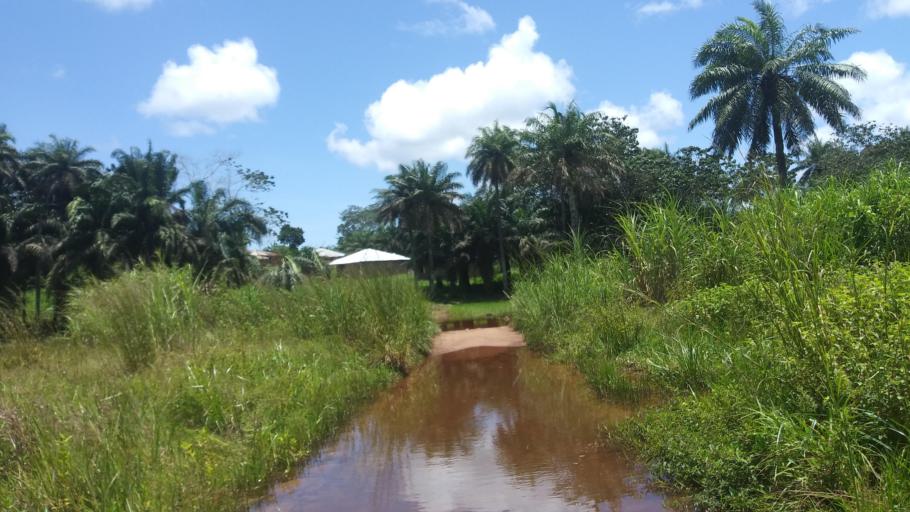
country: SL
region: Northern Province
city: Binkolo
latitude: 8.9003
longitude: -11.9915
